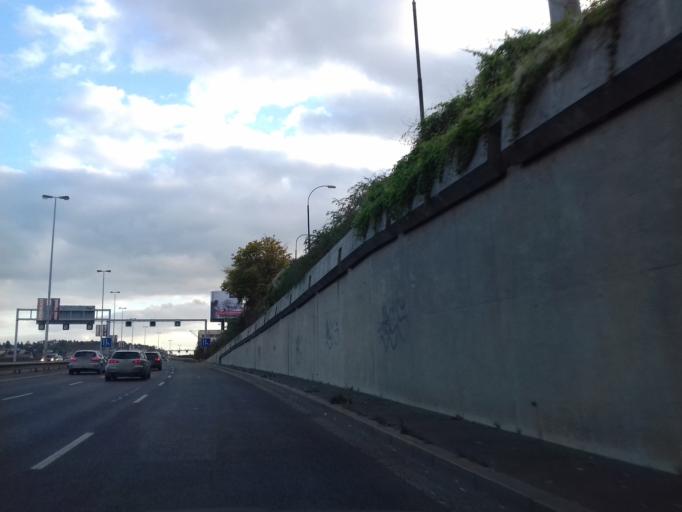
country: CZ
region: Praha
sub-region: Praha 2
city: Vysehrad
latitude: 50.0561
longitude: 14.4069
